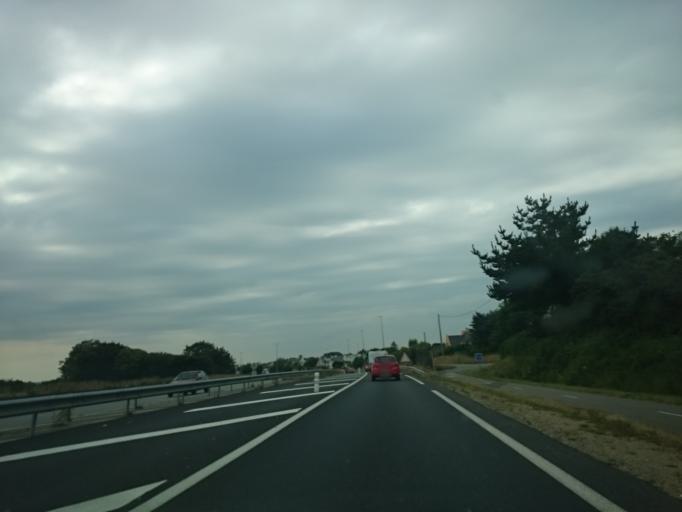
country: FR
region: Brittany
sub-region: Departement du Finistere
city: Guilers
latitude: 48.4191
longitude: -4.5508
